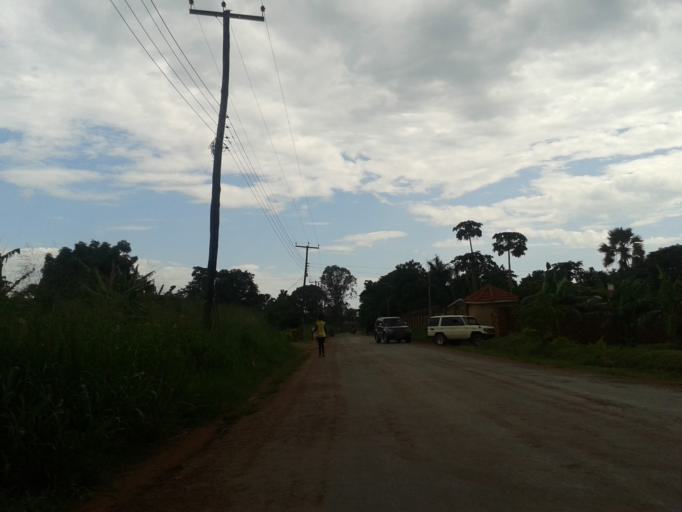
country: UG
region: Northern Region
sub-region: Gulu District
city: Gulu
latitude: 2.7836
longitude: 32.3067
